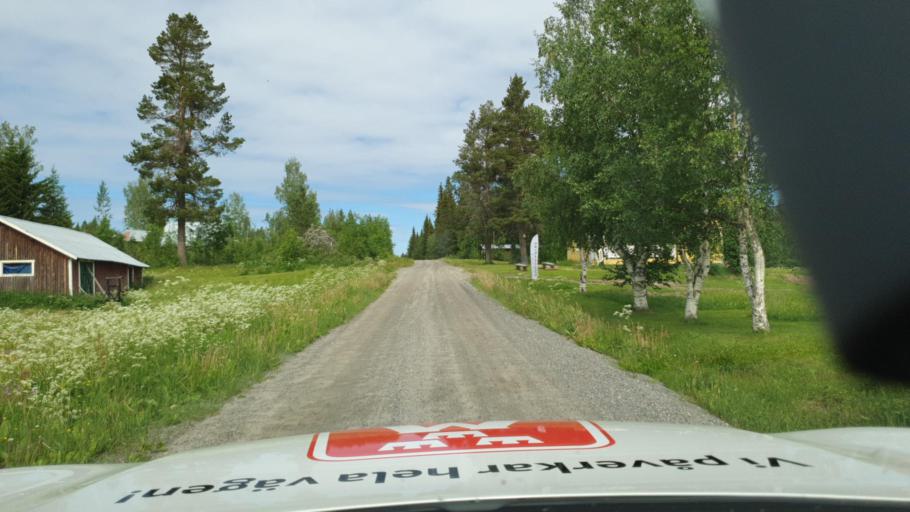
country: SE
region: Vaesterbotten
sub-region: Skelleftea Kommun
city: Langsele
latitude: 64.6198
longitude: 20.2653
